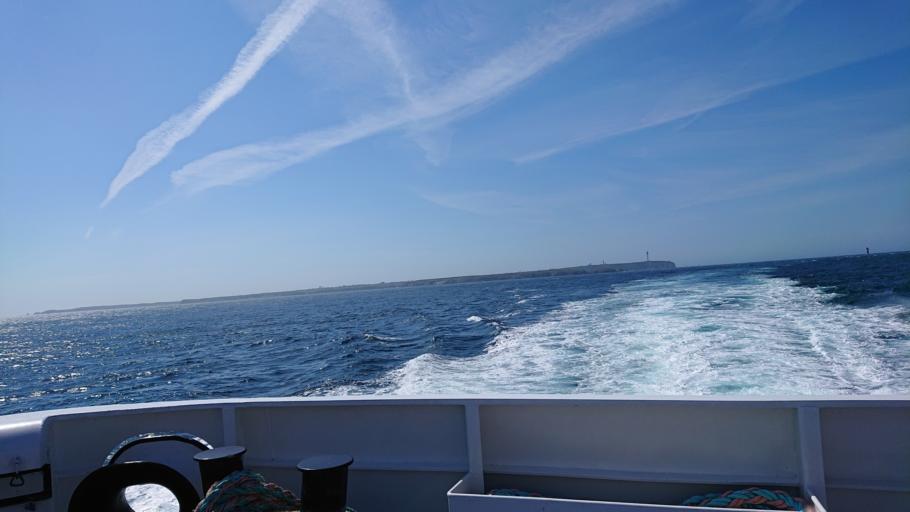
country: FR
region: Brittany
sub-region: Departement du Finistere
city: Porspoder
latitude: 48.4501
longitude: -5.0054
